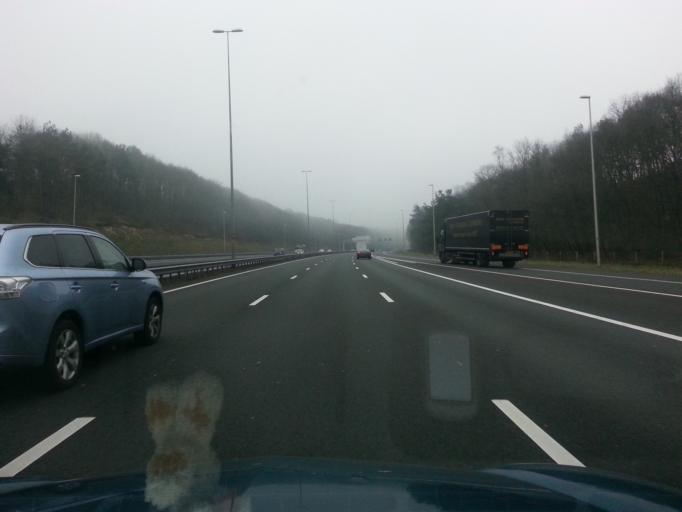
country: NL
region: Gelderland
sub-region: Gemeente Rozendaal
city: Rozendaal
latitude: 52.0141
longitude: 5.9332
